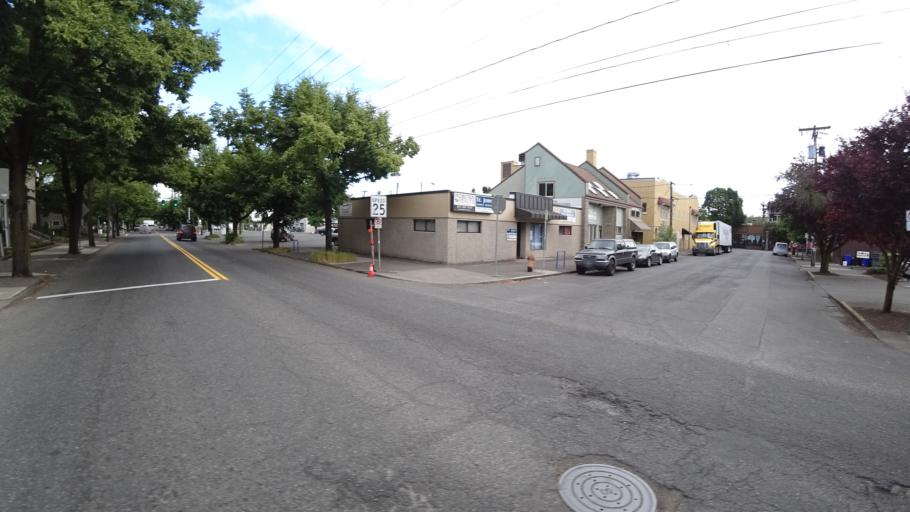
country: US
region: Oregon
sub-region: Washington County
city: West Haven
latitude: 45.5901
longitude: -122.7561
